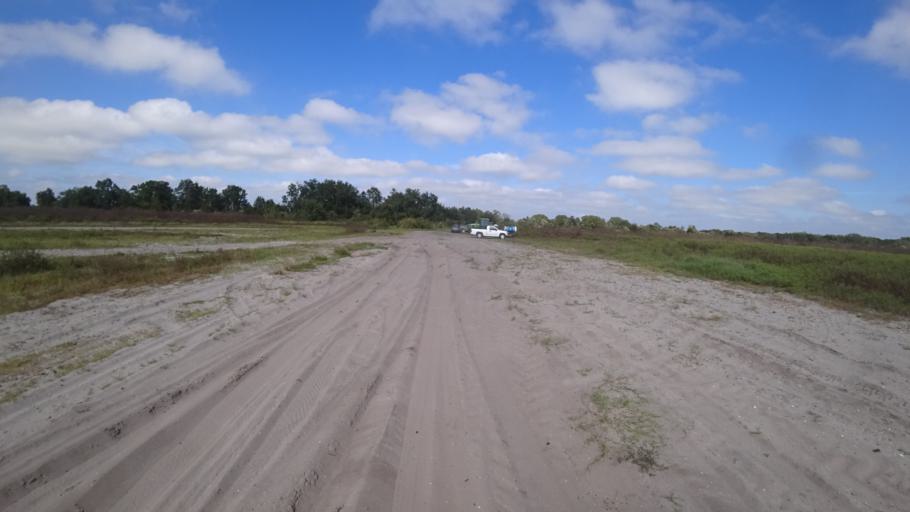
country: US
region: Florida
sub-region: DeSoto County
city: Arcadia
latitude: 27.2914
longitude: -82.0744
